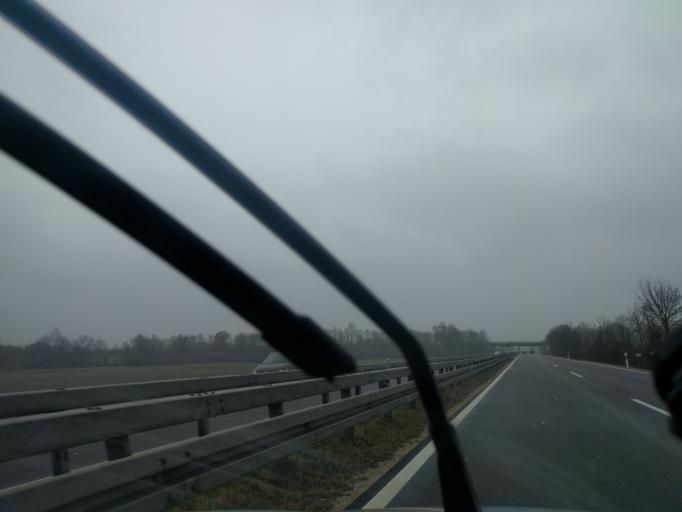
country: DE
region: Bavaria
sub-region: Swabia
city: Mertingen
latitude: 48.6564
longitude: 10.8317
